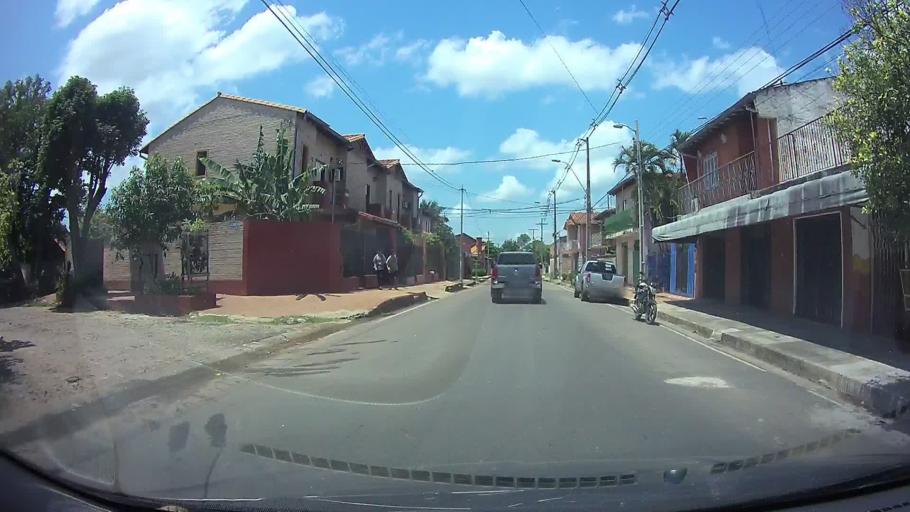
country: PY
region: Central
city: Fernando de la Mora
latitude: -25.3029
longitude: -57.5510
